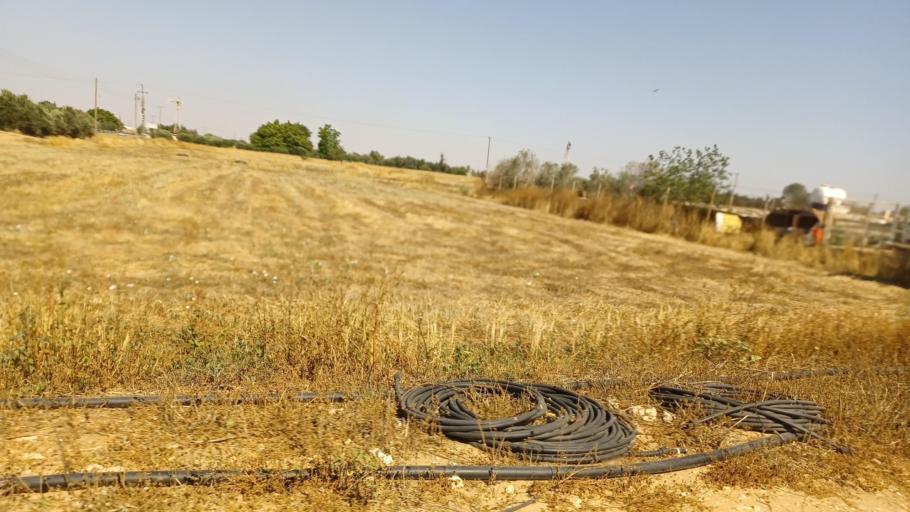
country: CY
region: Ammochostos
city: Frenaros
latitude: 35.0362
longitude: 33.9386
